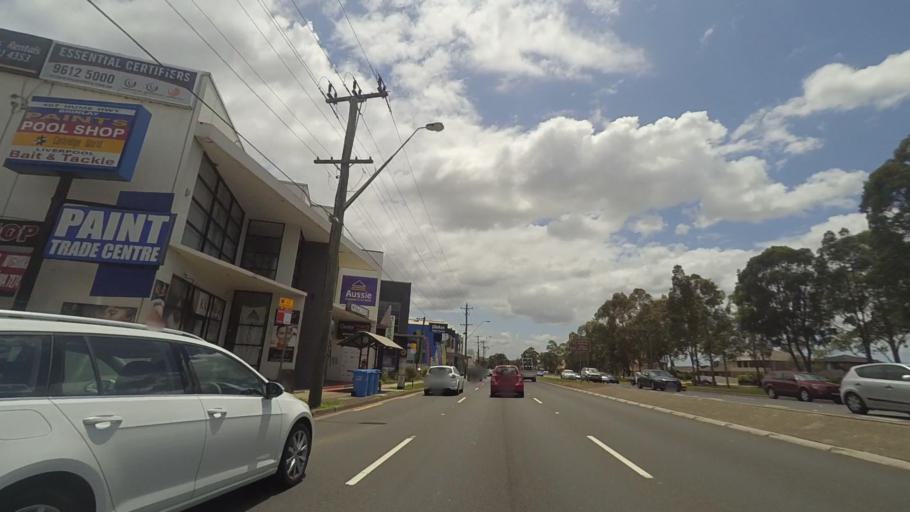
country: AU
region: New South Wales
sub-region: Liverpool
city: Miller
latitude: -33.9362
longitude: 150.9147
